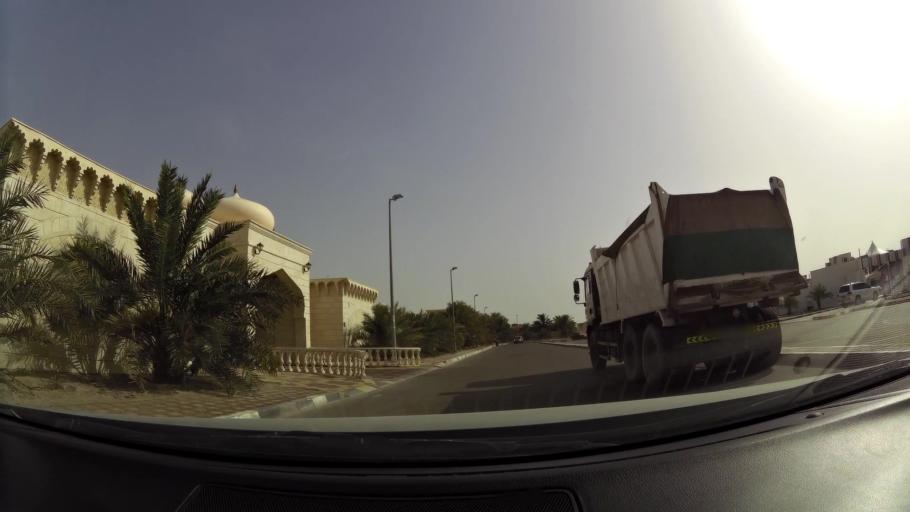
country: AE
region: Abu Dhabi
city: Al Ain
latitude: 24.1379
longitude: 55.7056
